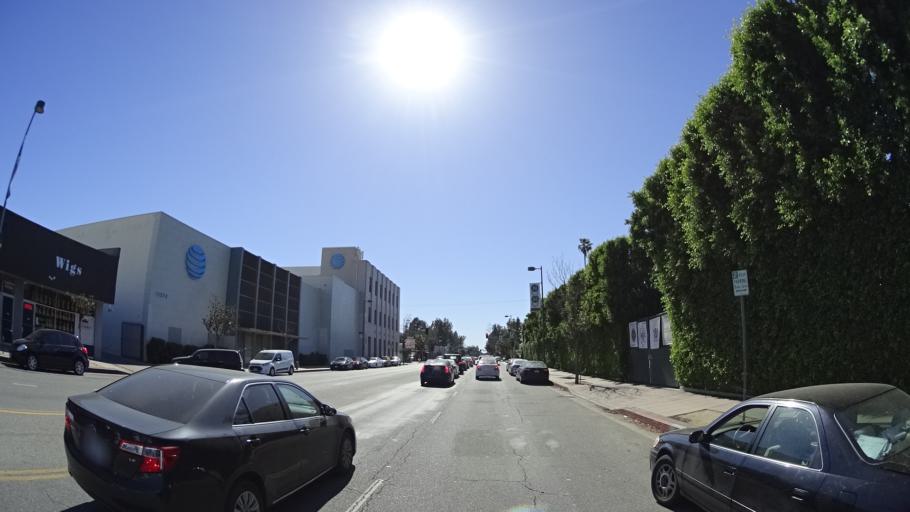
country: US
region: California
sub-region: Los Angeles County
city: North Hollywood
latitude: 34.1650
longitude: -118.3764
